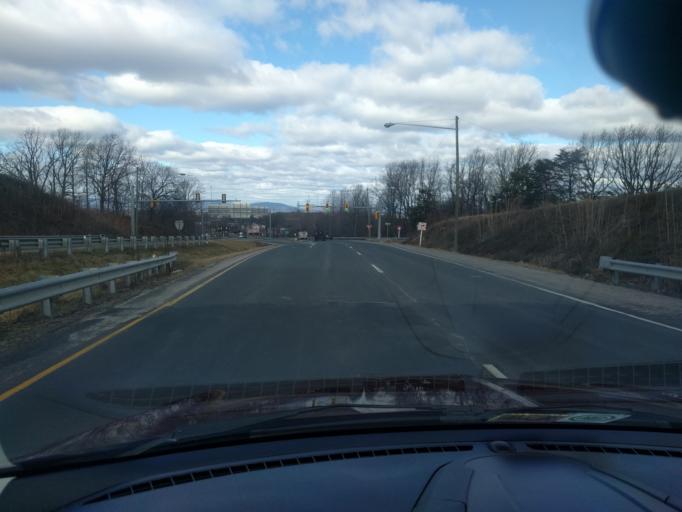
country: US
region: Virginia
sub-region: City of Lynchburg
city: Lynchburg
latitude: 37.3787
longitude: -79.1304
